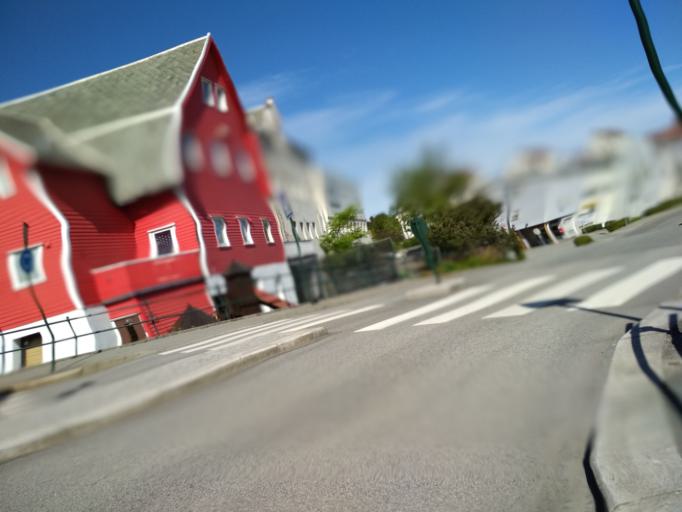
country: NO
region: Rogaland
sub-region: Stavanger
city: Stavanger
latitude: 58.9745
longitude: 5.7122
